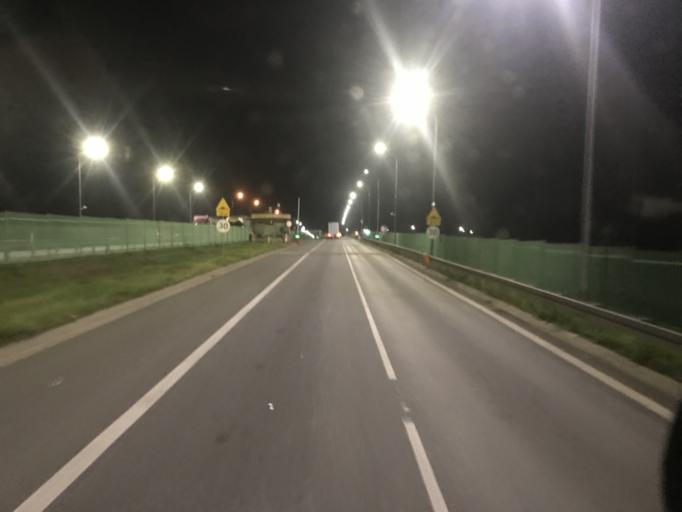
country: PL
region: Lublin Voivodeship
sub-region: Powiat bialski
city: Terespol
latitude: 52.1140
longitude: 23.5642
